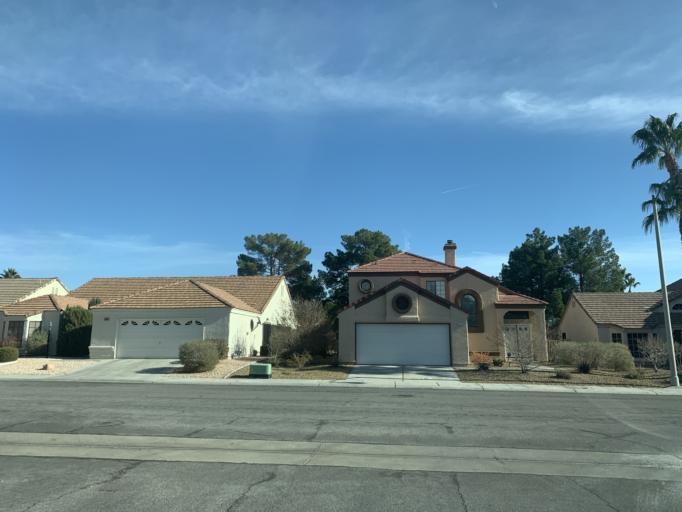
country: US
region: Nevada
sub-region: Clark County
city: Summerlin South
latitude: 36.1348
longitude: -115.2963
